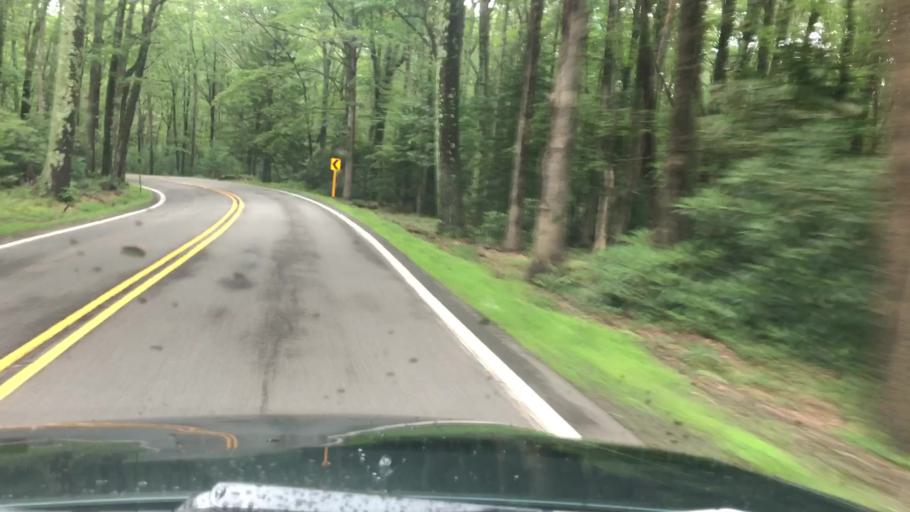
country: US
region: Pennsylvania
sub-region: Monroe County
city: Mountainhome
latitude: 41.3001
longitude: -75.2125
